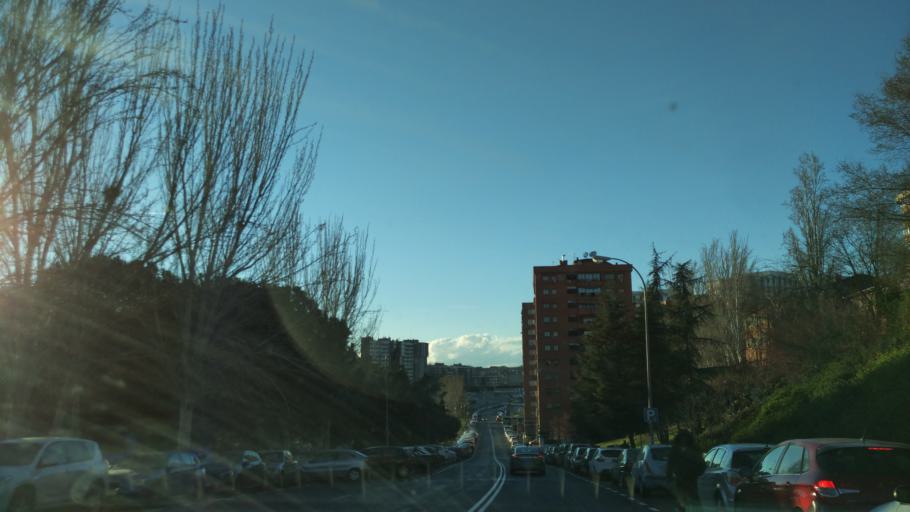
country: ES
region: Madrid
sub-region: Provincia de Madrid
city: Pinar de Chamartin
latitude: 40.4848
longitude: -3.6901
